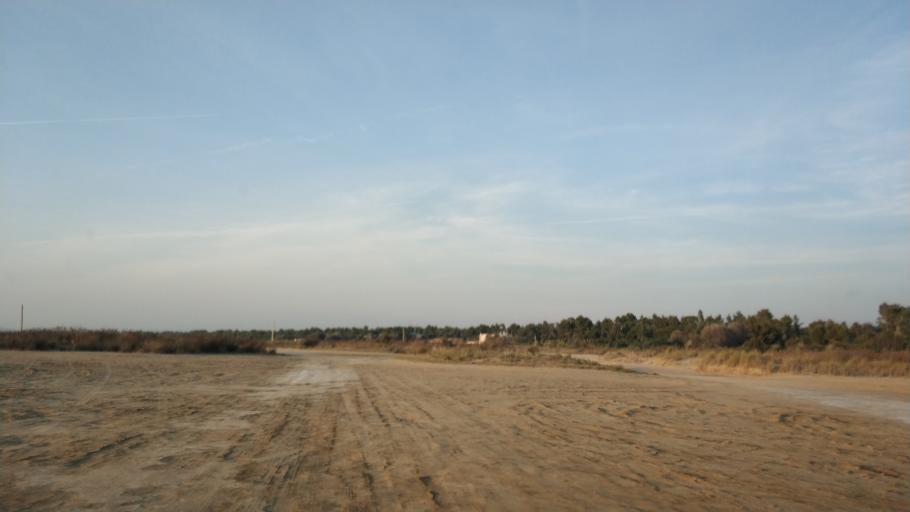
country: AL
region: Fier
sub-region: Rrethi i Lushnjes
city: Divjake
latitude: 40.9658
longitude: 19.4751
